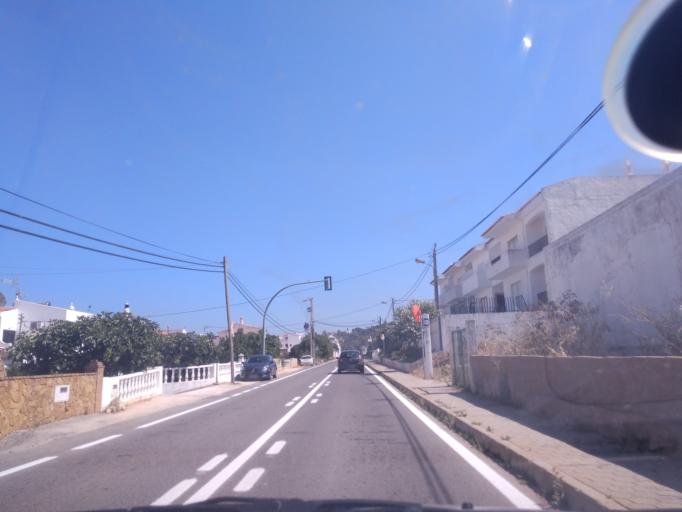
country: PT
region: Faro
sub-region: Lagos
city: Lagos
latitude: 37.1238
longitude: -8.6947
